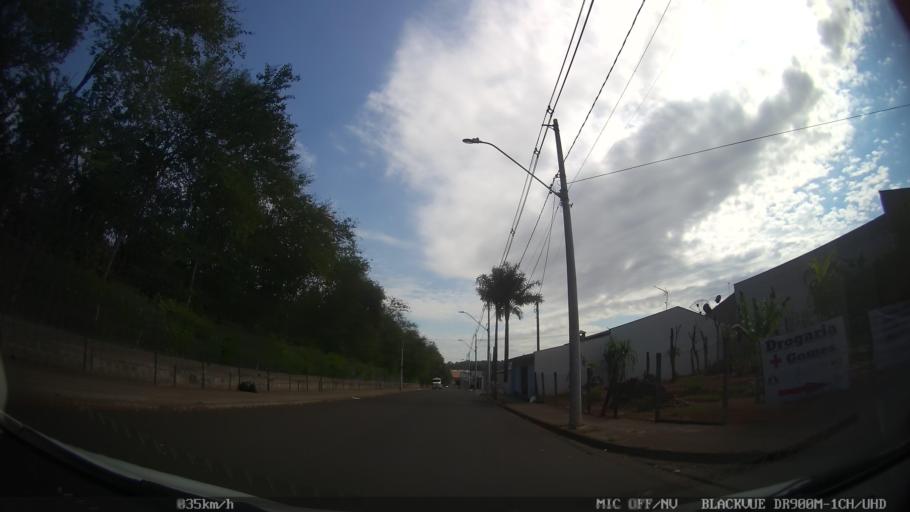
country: BR
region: Sao Paulo
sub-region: Americana
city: Americana
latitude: -22.7131
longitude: -47.3174
